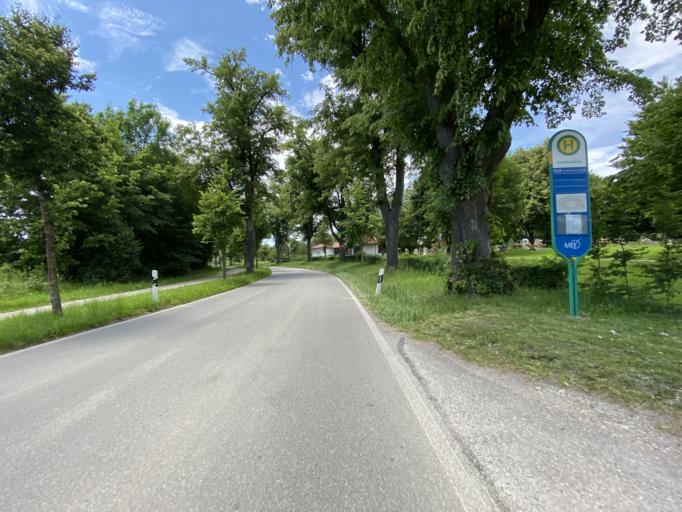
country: DE
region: Bavaria
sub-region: Upper Bavaria
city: Seefeld
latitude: 48.0436
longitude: 11.2046
